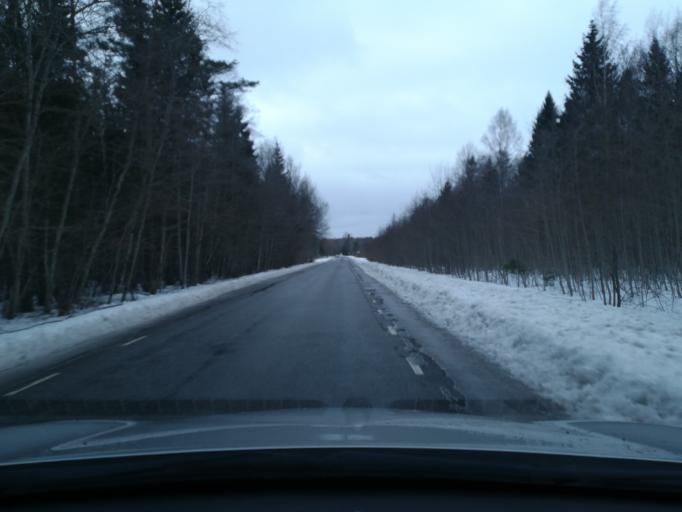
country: EE
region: Harju
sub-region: Nissi vald
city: Turba
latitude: 59.0692
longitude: 24.2505
